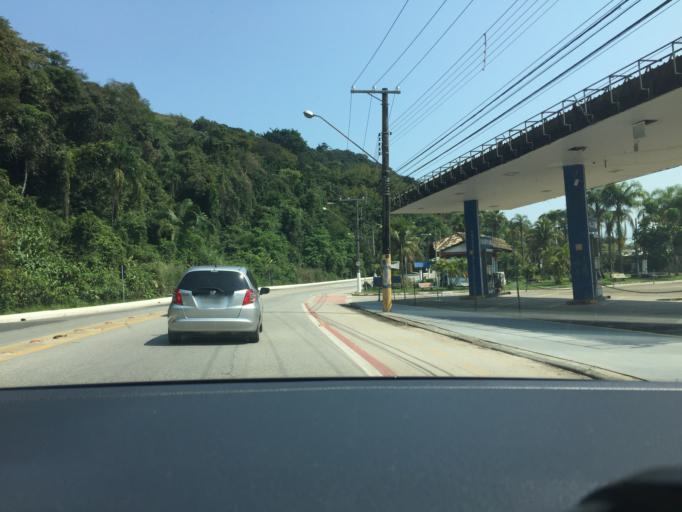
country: BR
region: Sao Paulo
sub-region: Guaruja
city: Guaruja
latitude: -23.9785
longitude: -46.1897
